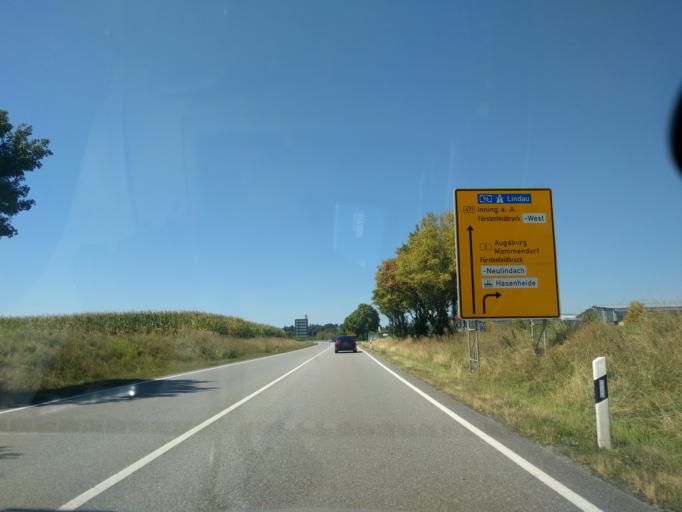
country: DE
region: Bavaria
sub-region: Upper Bavaria
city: Fuerstenfeldbruck
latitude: 48.1852
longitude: 11.2412
